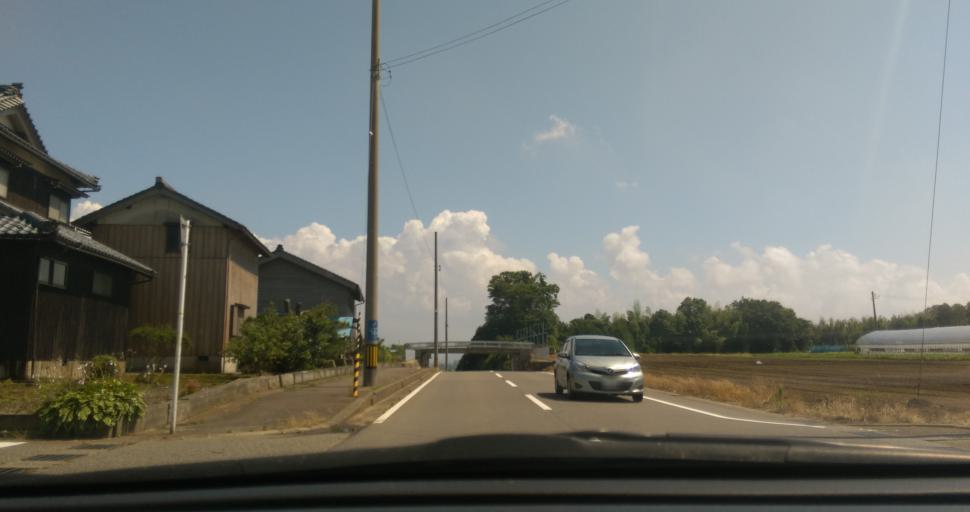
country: JP
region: Fukui
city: Mikuni
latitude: 36.2278
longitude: 136.1647
